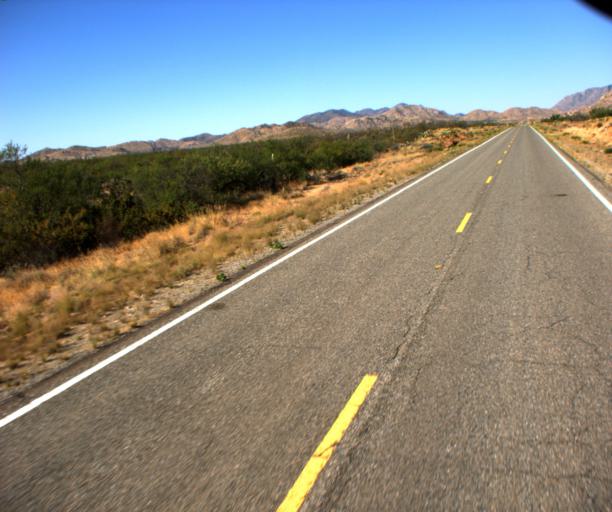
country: US
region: Arizona
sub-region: Graham County
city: Swift Trail Junction
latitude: 32.5915
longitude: -109.6937
